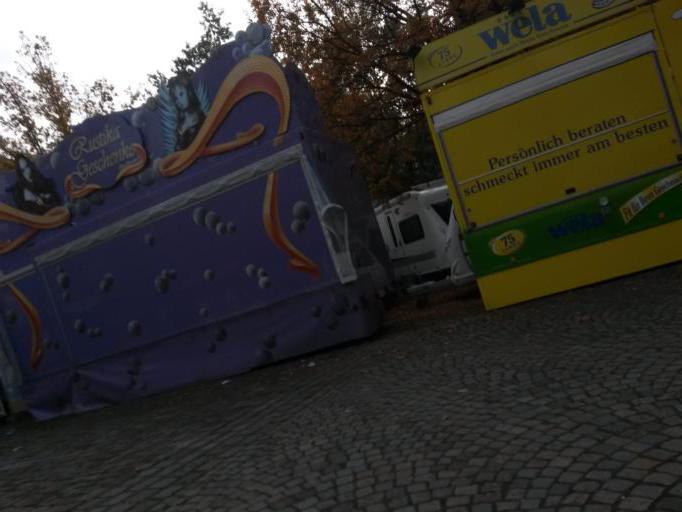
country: DE
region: Bremen
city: Bremen
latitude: 53.0880
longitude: 8.8090
